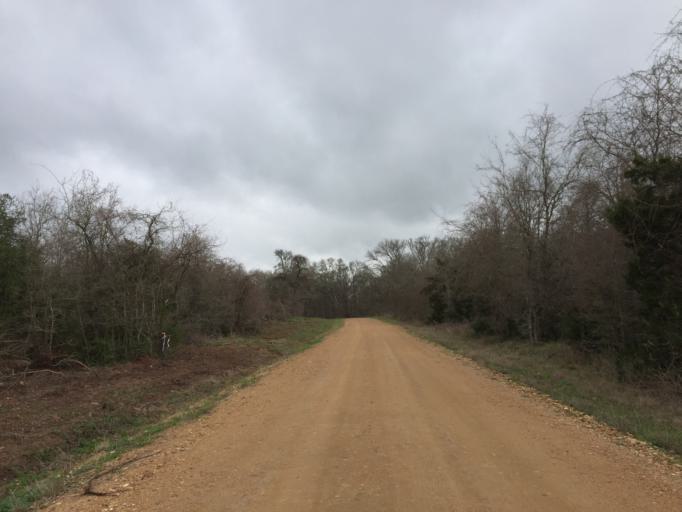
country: US
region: Texas
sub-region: Bastrop County
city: Bastrop
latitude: 30.0845
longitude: -97.3237
